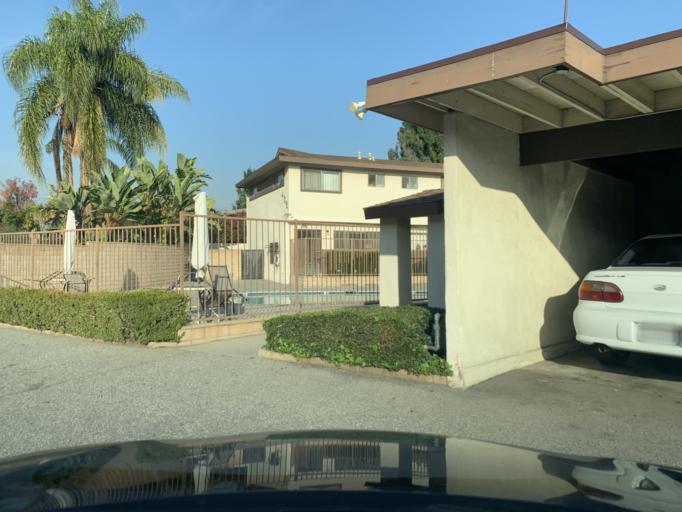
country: US
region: California
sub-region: Los Angeles County
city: Covina
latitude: 34.0912
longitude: -117.8977
